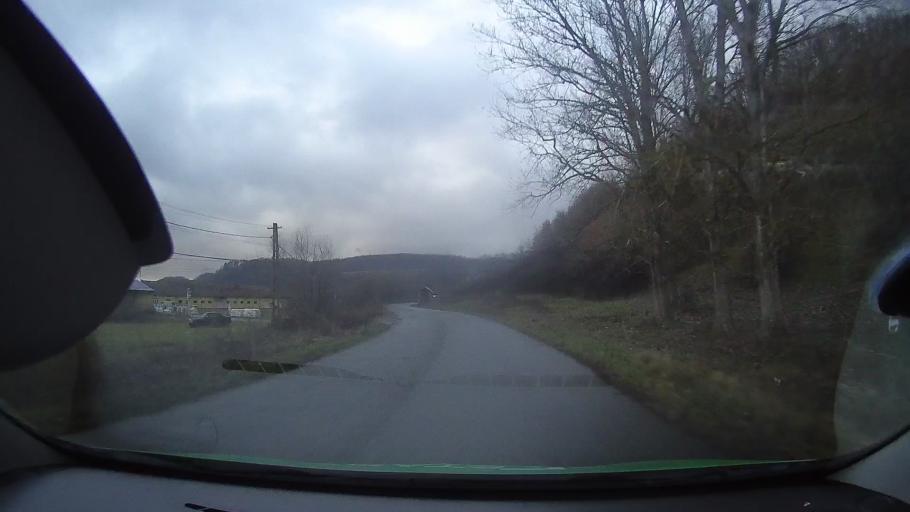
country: RO
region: Hunedoara
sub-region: Comuna Baia de Cris
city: Baia de Cris
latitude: 46.1874
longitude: 22.7133
